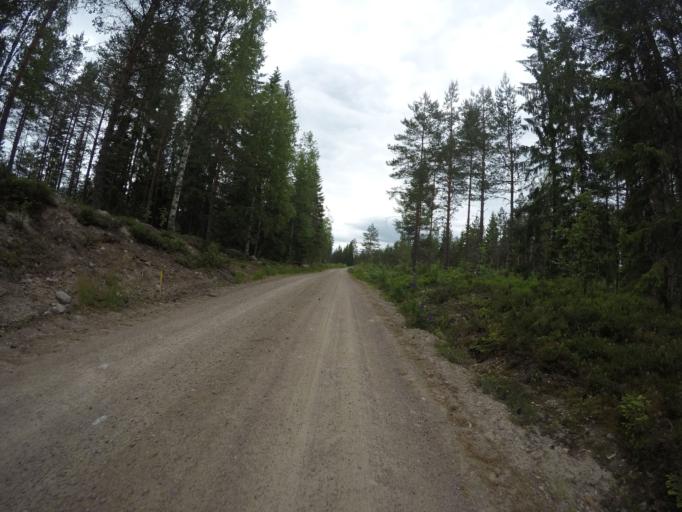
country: SE
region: Dalarna
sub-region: Ludvika Kommun
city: Abborrberget
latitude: 60.0953
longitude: 14.5466
